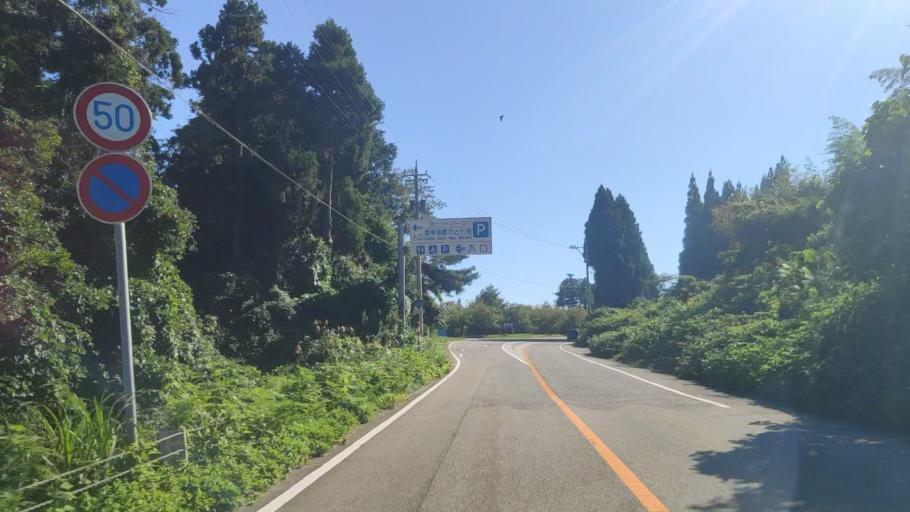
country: JP
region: Ishikawa
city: Nanao
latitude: 37.2687
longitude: 137.0946
